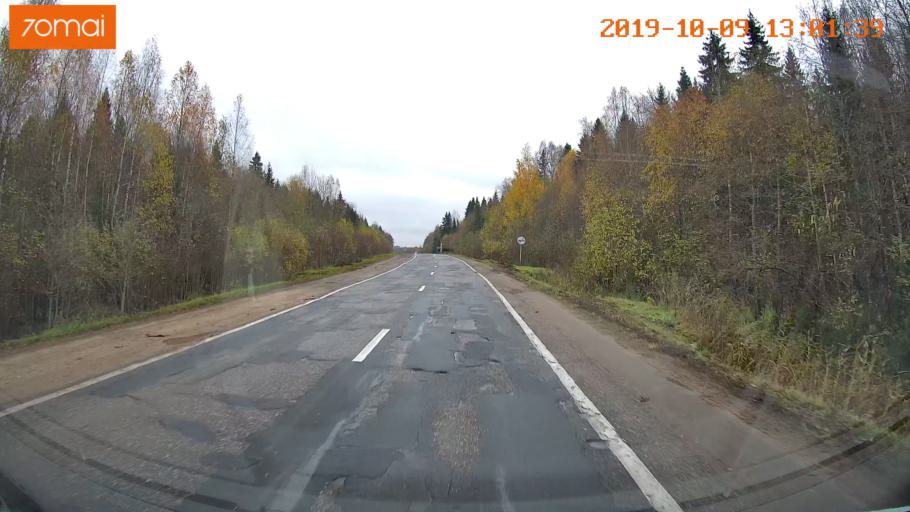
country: RU
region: Jaroslavl
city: Prechistoye
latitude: 58.3667
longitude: 40.4885
